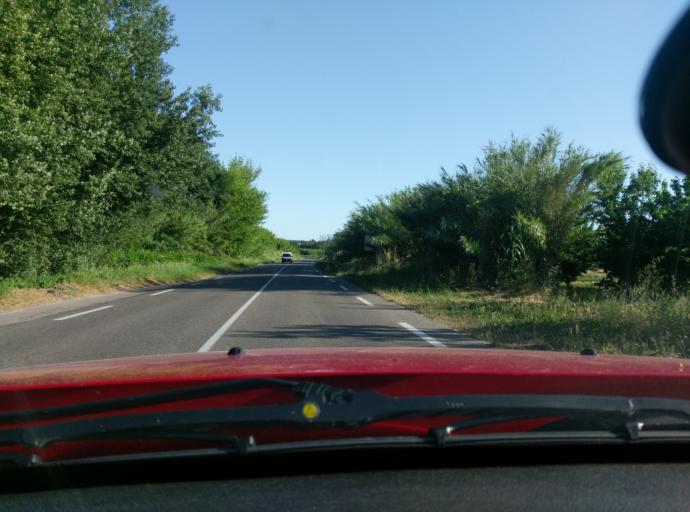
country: FR
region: Languedoc-Roussillon
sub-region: Departement du Gard
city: Remoulins
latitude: 43.9474
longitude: 4.5593
